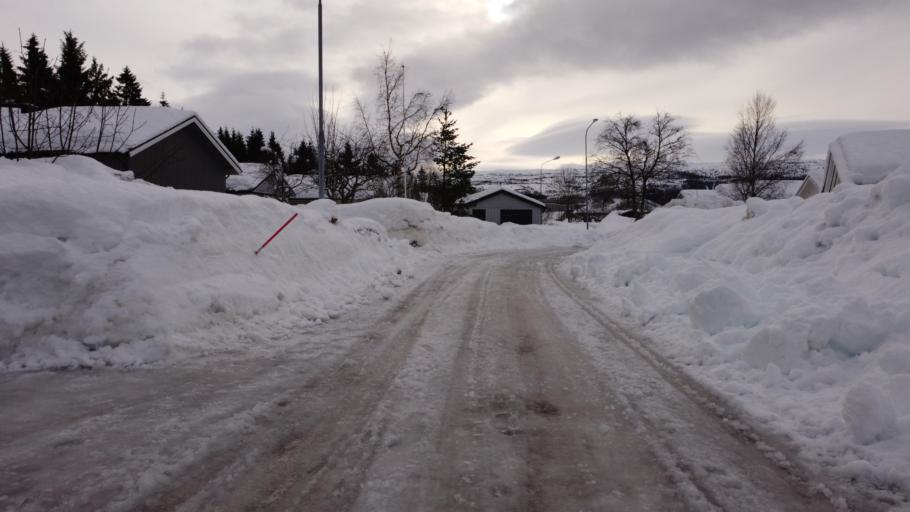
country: NO
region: Nordland
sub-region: Rana
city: Mo i Rana
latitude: 66.3340
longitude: 14.1556
